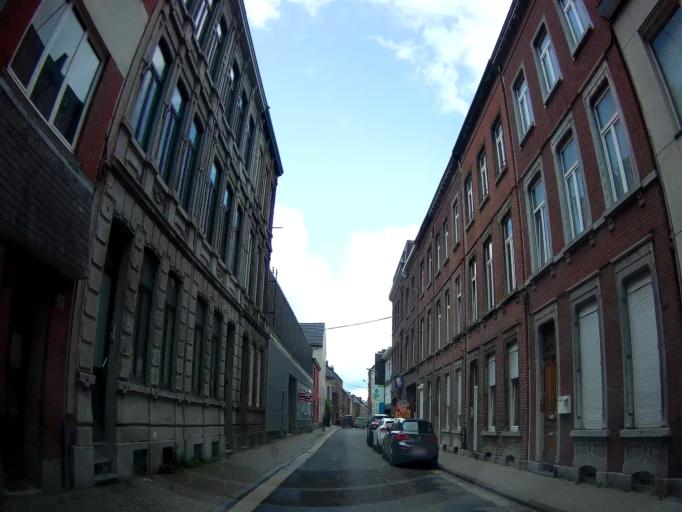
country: BE
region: Wallonia
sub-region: Province de Liege
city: Verviers
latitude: 50.5890
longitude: 5.8712
